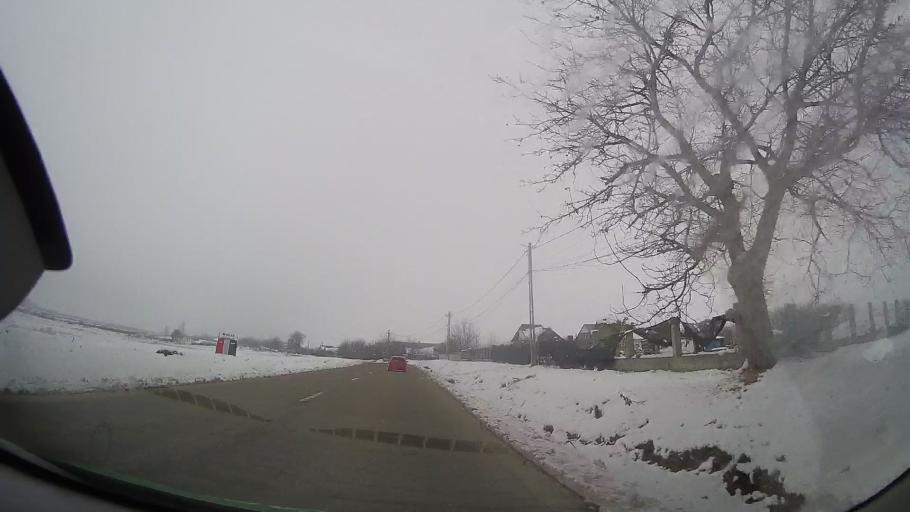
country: RO
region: Vaslui
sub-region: Comuna Negresti
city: Negresti
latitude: 46.8391
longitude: 27.4334
